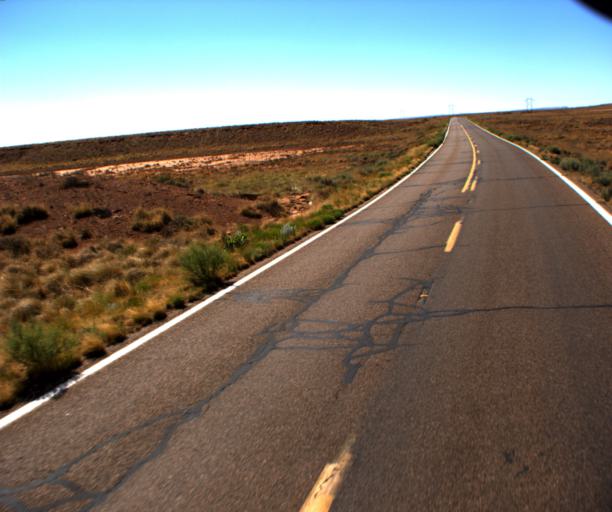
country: US
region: Arizona
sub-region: Coconino County
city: LeChee
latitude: 35.2621
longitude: -110.9690
